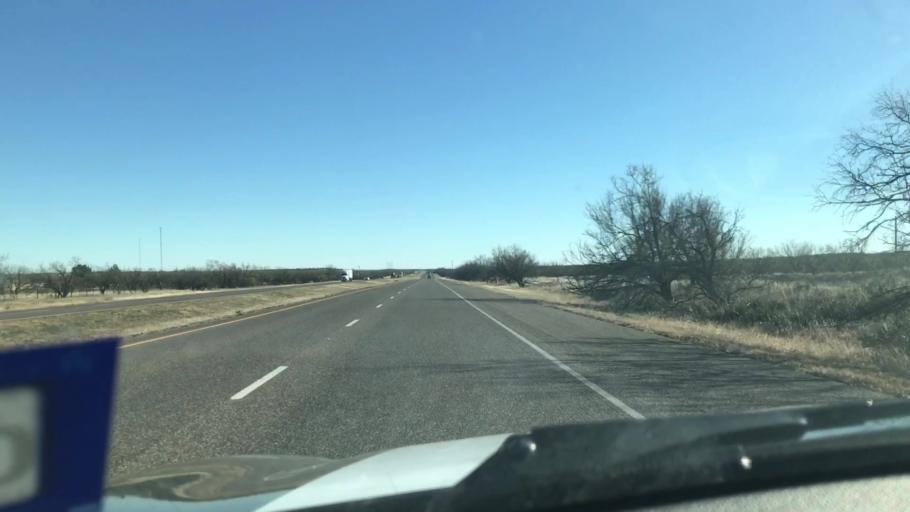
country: US
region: Texas
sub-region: Scurry County
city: Snyder
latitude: 32.8300
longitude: -100.9849
